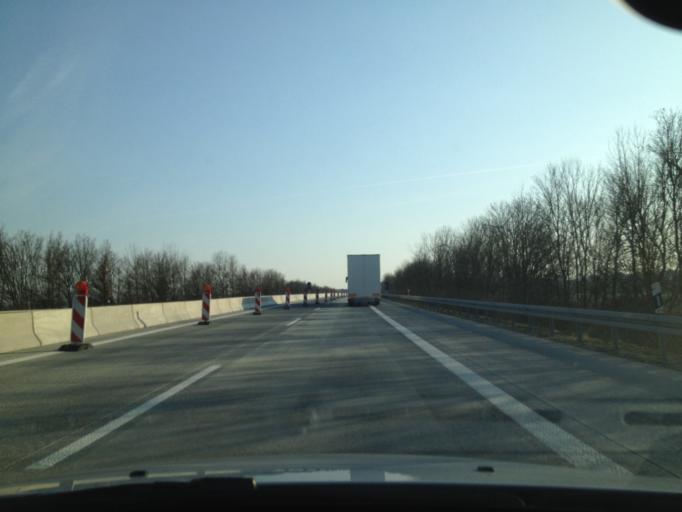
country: DE
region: Bavaria
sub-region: Regierungsbezirk Mittelfranken
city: Gollhofen
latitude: 49.5937
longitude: 10.1742
